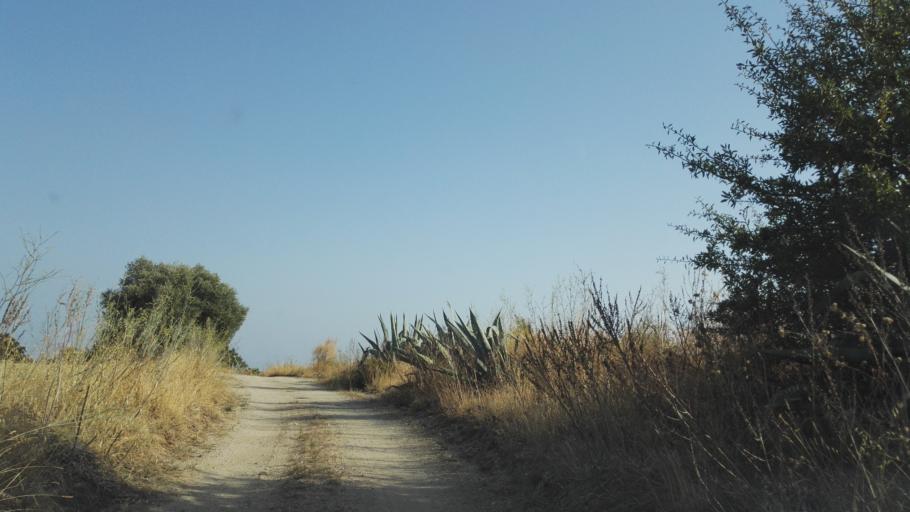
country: IT
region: Calabria
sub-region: Provincia di Reggio Calabria
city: Riace Marina
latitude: 38.3735
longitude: 16.4958
